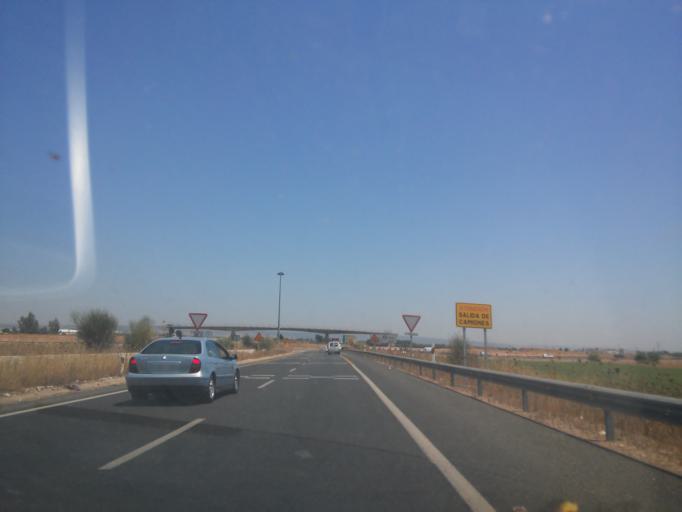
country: ES
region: Andalusia
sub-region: Provincia de Sevilla
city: La Rinconada
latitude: 37.4652
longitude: -5.9677
